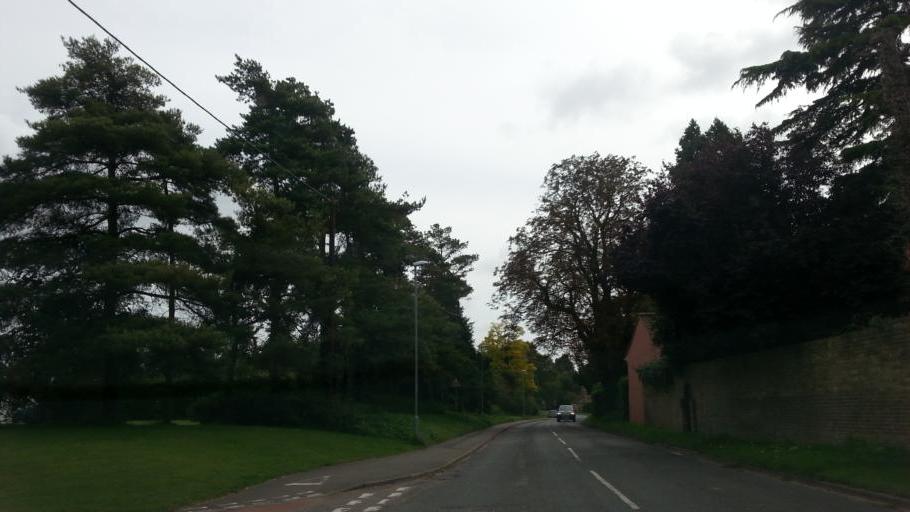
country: GB
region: England
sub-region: Cambridgeshire
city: Barton
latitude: 52.1836
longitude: 0.0525
